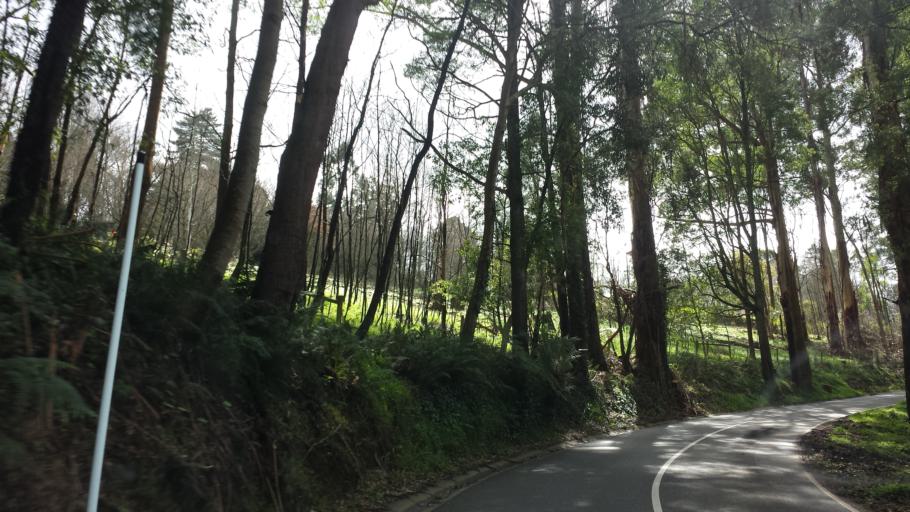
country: AU
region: Victoria
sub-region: Yarra Ranges
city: Kallista
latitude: -37.8838
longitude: 145.3640
